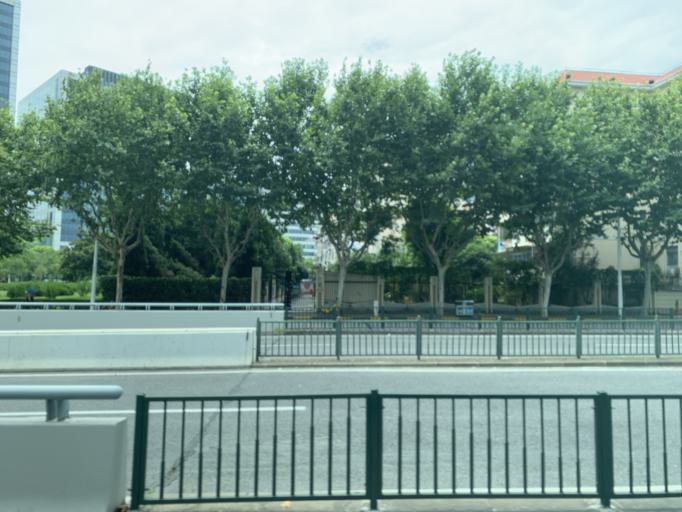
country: CN
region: Shanghai Shi
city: Pudong
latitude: 31.2339
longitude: 121.5198
